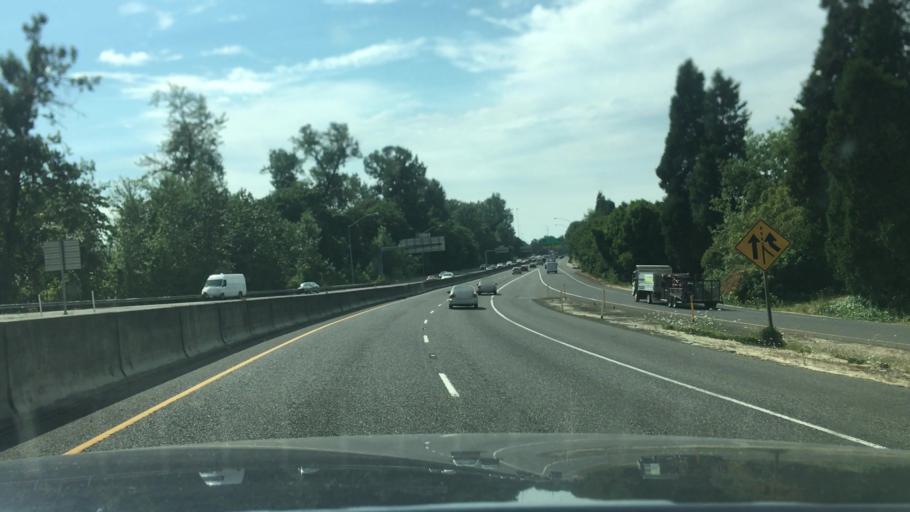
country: US
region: Oregon
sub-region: Lane County
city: Eugene
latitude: 44.0612
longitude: -123.0869
